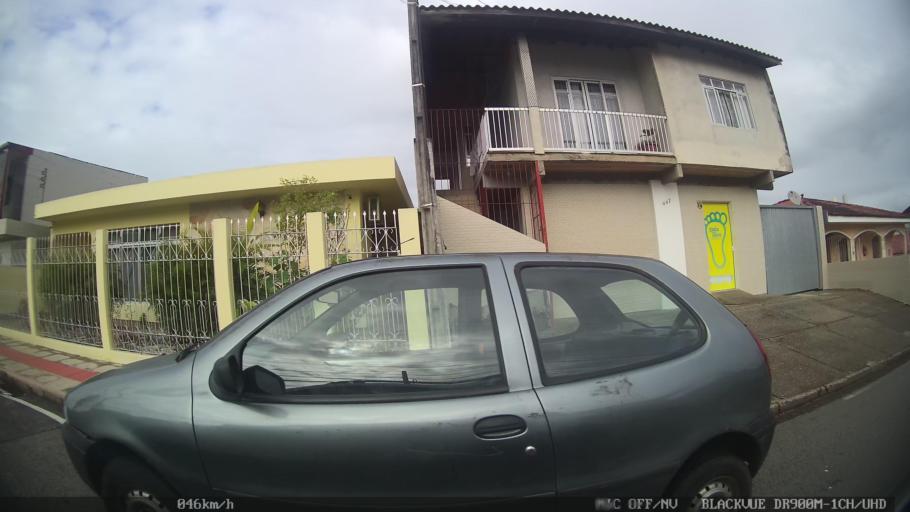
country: BR
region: Santa Catarina
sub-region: Sao Jose
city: Campinas
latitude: -27.5427
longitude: -48.6235
